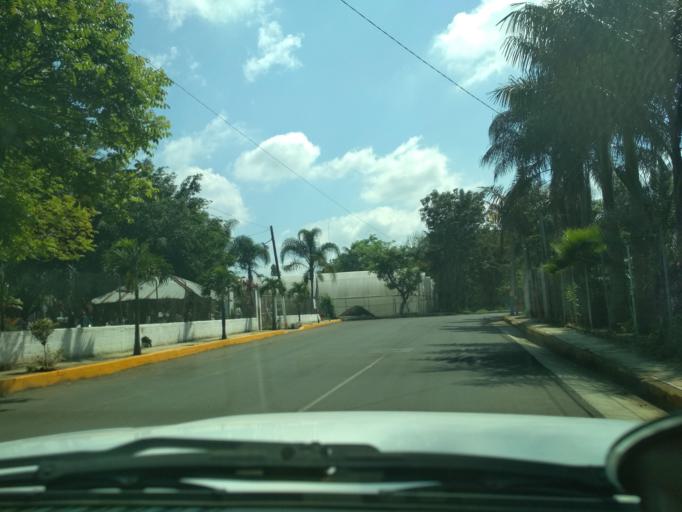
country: MX
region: Veracruz
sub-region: Fortin
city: Fraccionamiento los Alamos
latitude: 18.9171
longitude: -96.9762
